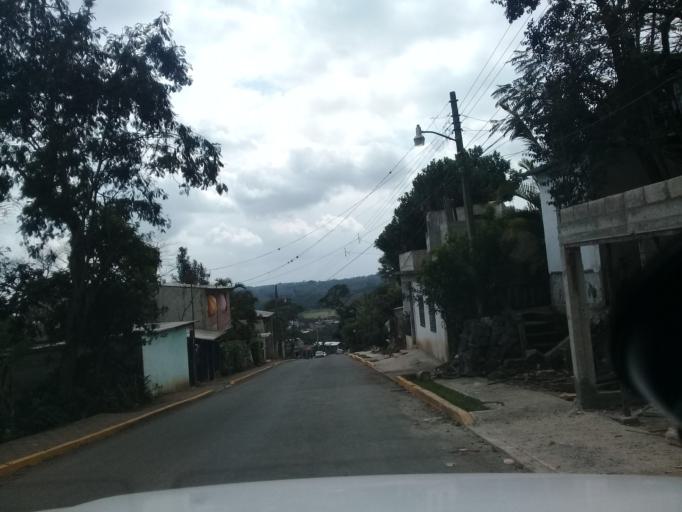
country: MX
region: Veracruz
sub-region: Xalapa
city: Fraccionamiento las Fuentes
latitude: 19.4783
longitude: -96.8774
